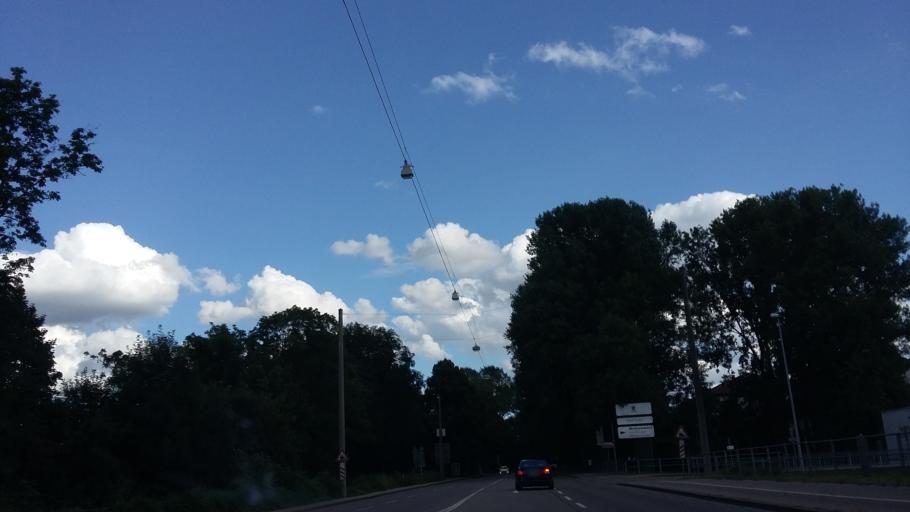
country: DE
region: Bavaria
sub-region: Swabia
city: Augsburg
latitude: 48.3807
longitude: 10.9045
